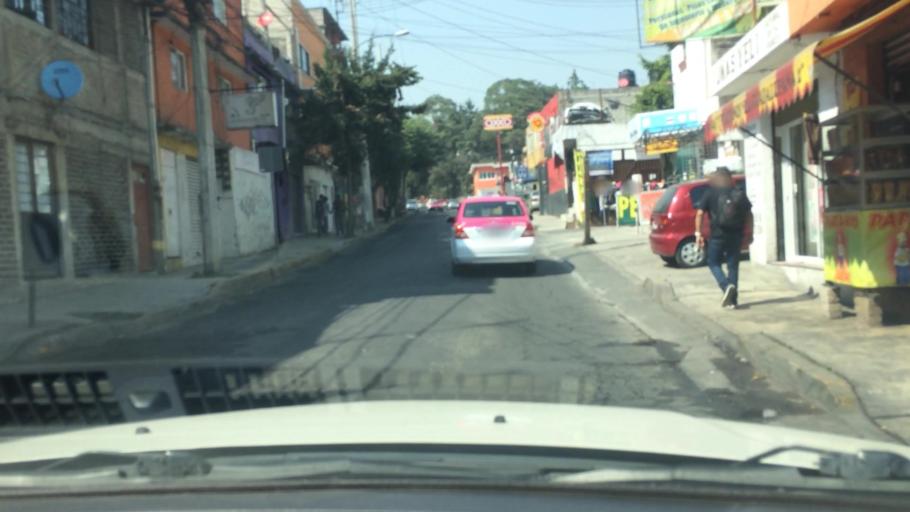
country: MX
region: Mexico City
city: Tlalpan
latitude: 19.2744
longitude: -99.1619
